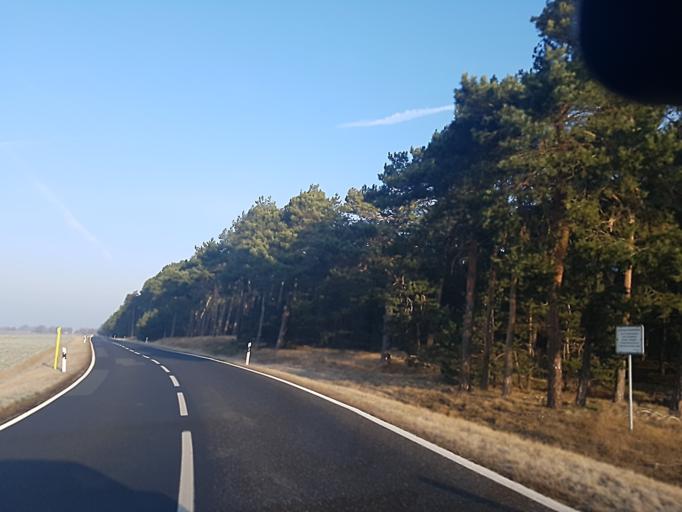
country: DE
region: Brandenburg
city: Bruck
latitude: 52.2333
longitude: 12.7120
